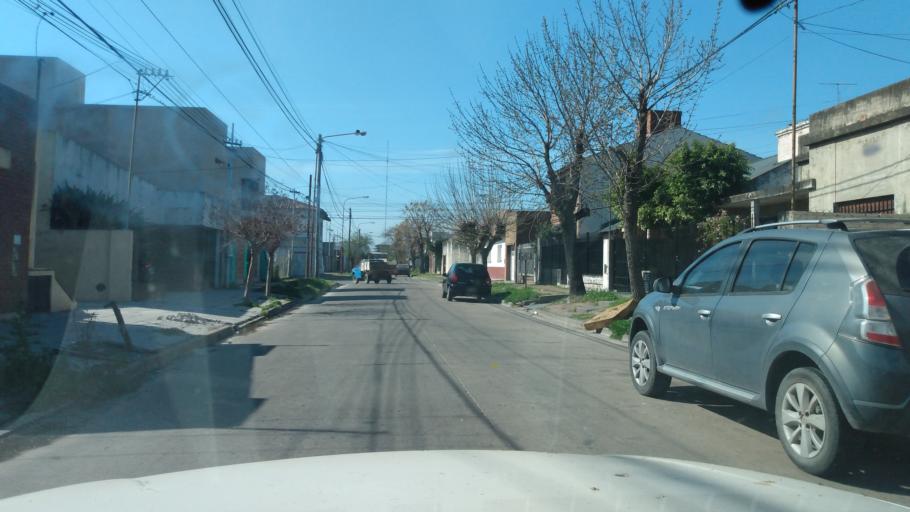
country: AR
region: Buenos Aires
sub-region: Partido de Lujan
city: Lujan
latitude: -34.5682
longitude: -59.0986
